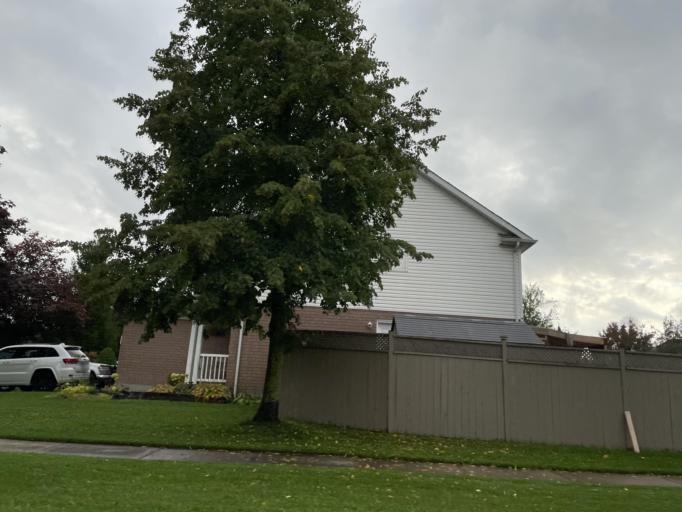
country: CA
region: Ontario
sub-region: Wellington County
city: Guelph
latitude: 43.5673
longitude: -80.2274
